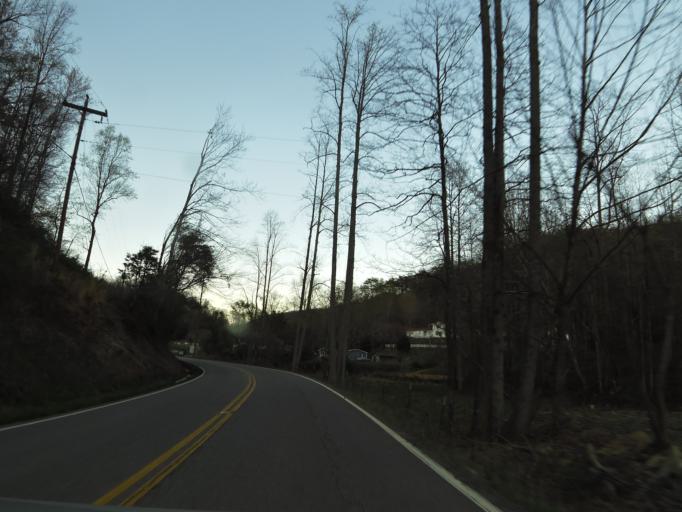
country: US
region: Tennessee
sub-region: Anderson County
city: Rocky Top
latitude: 36.1547
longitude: -84.1990
